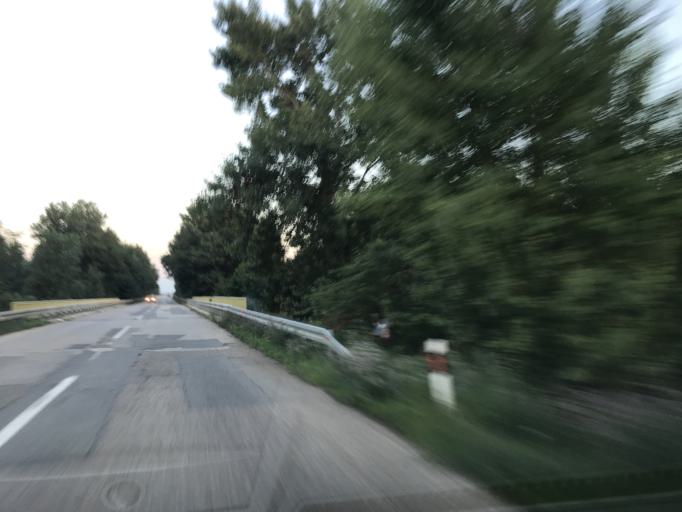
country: RS
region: Central Serbia
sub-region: Borski Okrug
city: Negotin
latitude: 44.2695
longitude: 22.5125
